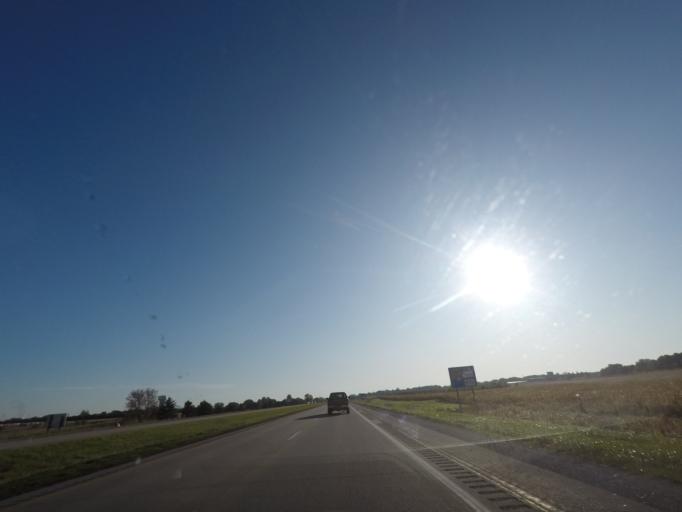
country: US
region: Iowa
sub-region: Story County
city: Ames
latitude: 42.0068
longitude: -93.6700
